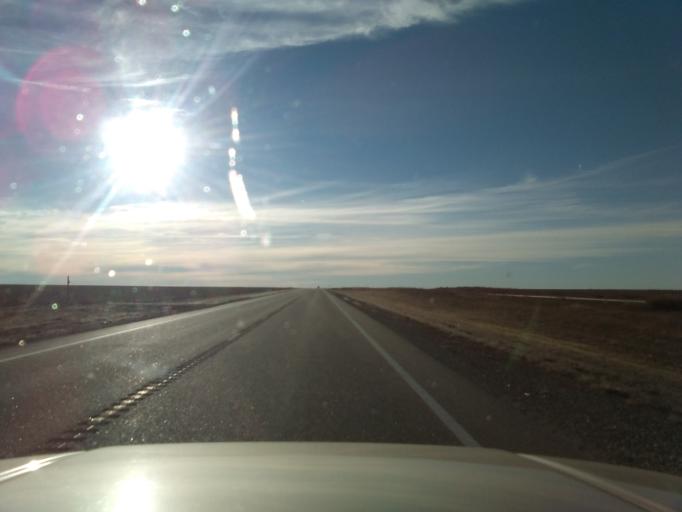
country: US
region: Kansas
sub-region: Sheridan County
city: Hoxie
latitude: 39.5293
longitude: -100.6021
